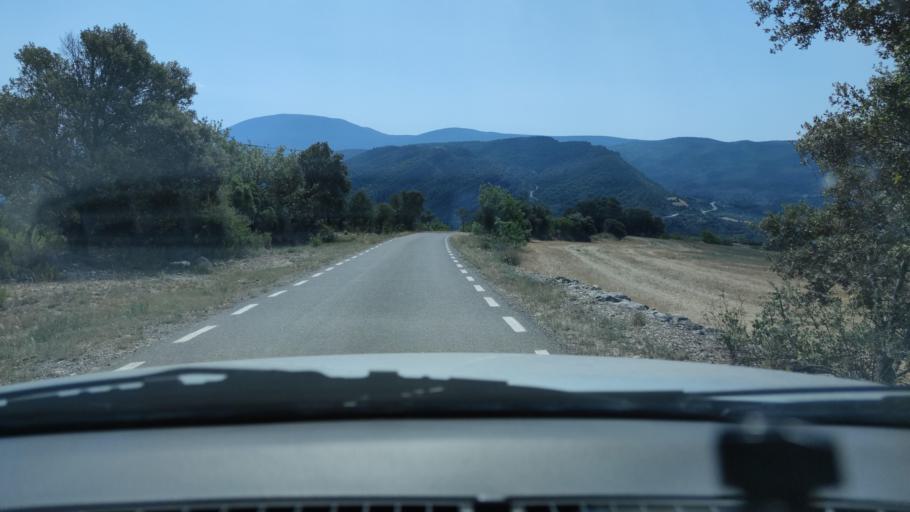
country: ES
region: Catalonia
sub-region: Provincia de Lleida
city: Ager
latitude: 42.0076
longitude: 0.8332
